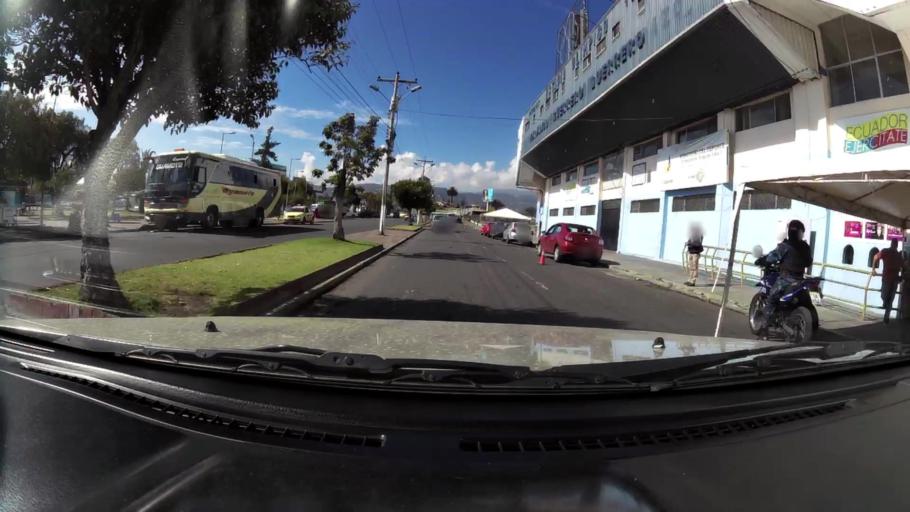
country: EC
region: Chimborazo
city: Riobamba
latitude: -1.6665
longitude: -78.6595
